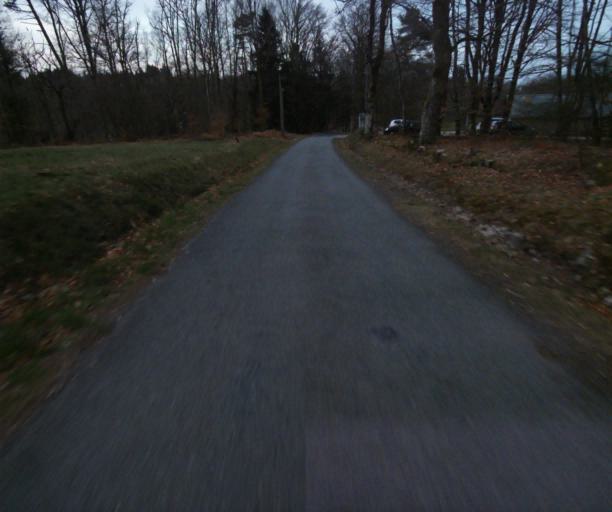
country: FR
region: Limousin
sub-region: Departement de la Correze
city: Correze
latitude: 45.4341
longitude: 1.8423
